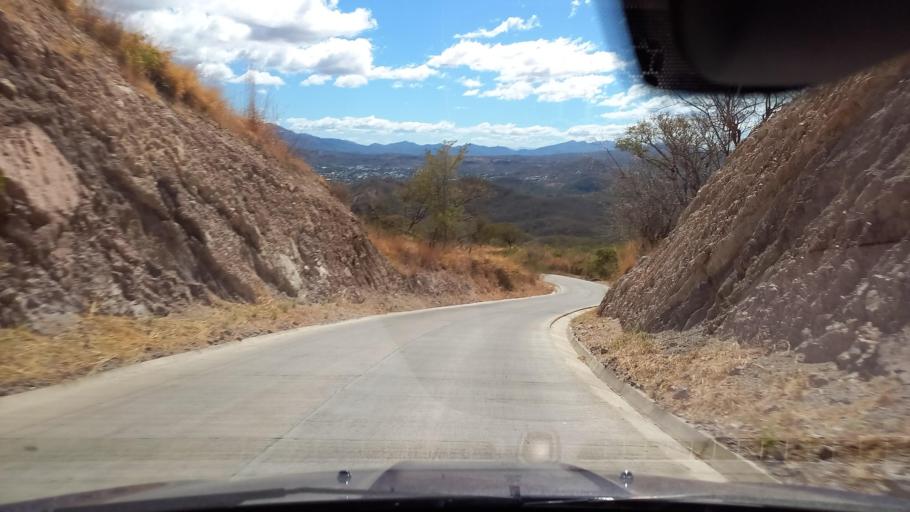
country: SV
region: Santa Ana
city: Metapan
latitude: 14.3652
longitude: -89.4837
